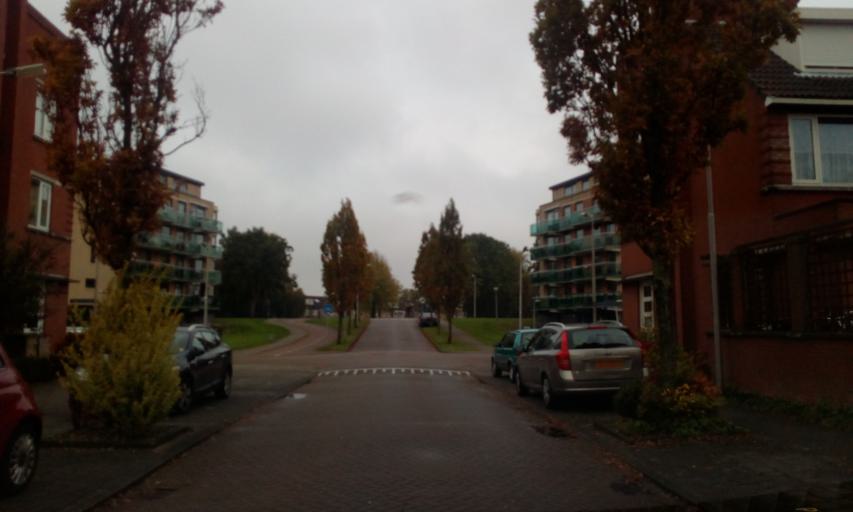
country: NL
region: South Holland
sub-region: Gemeente Lansingerland
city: Berkel en Rodenrijs
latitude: 51.9843
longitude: 4.4678
